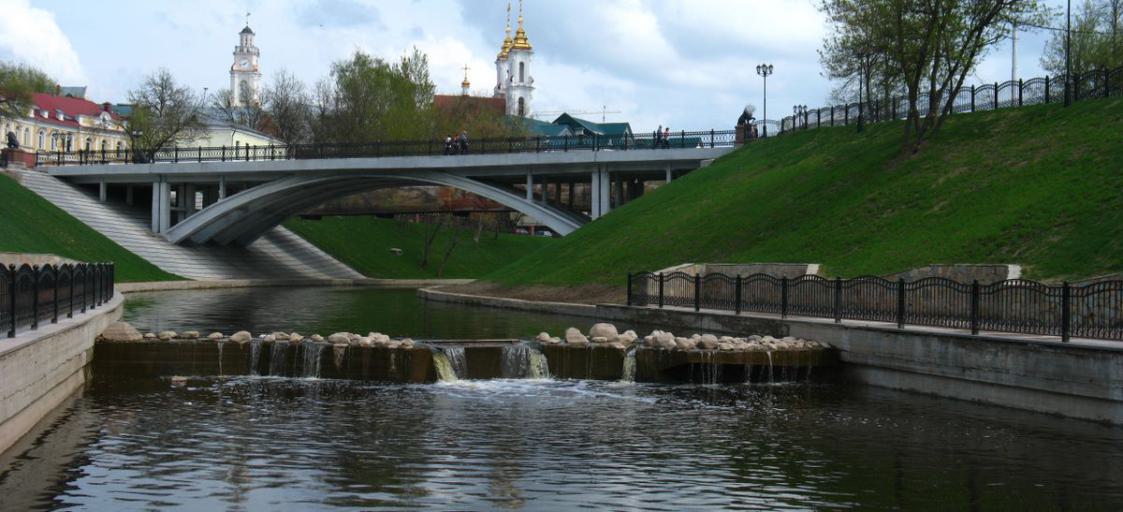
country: BY
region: Vitebsk
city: Vitebsk
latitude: 55.1945
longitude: 30.2007
